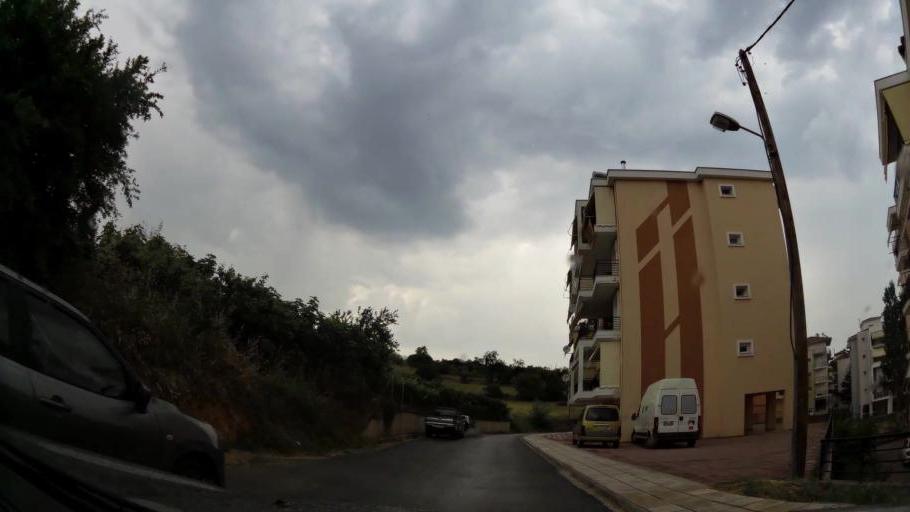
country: GR
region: Central Macedonia
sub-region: Nomos Imathias
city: Veroia
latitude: 40.5218
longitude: 22.1934
